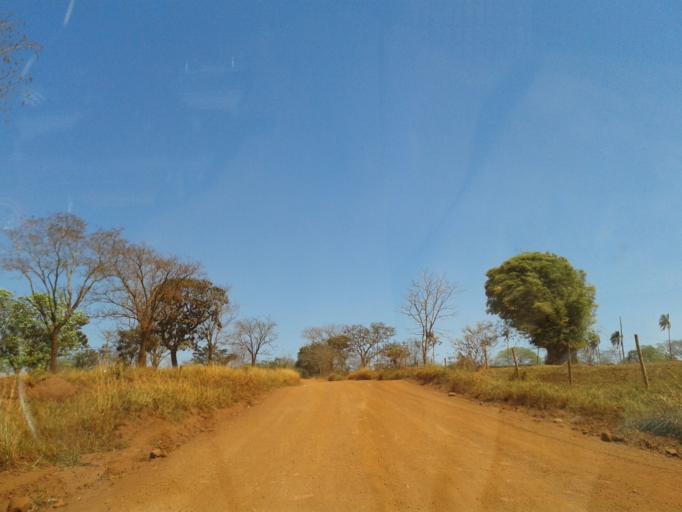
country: BR
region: Minas Gerais
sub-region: Ituiutaba
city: Ituiutaba
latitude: -18.9768
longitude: -49.4225
